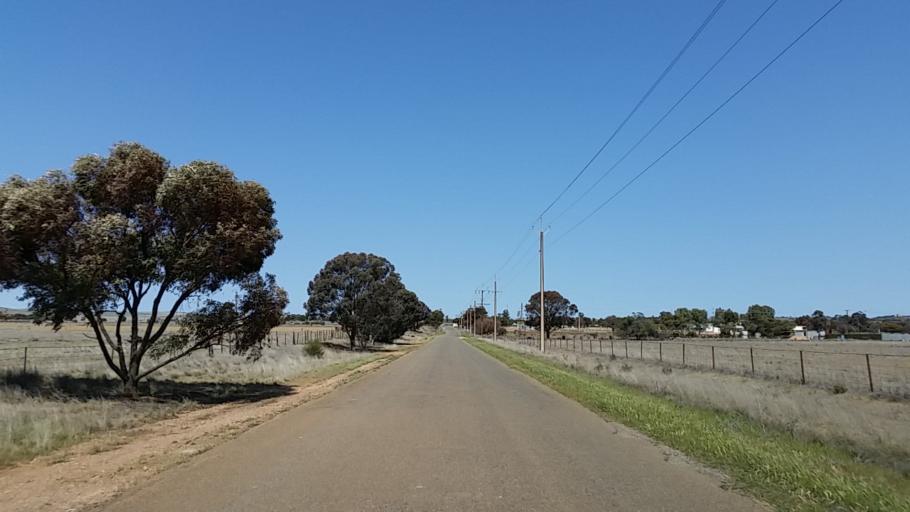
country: AU
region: South Australia
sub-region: Peterborough
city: Peterborough
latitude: -32.9659
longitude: 138.8466
